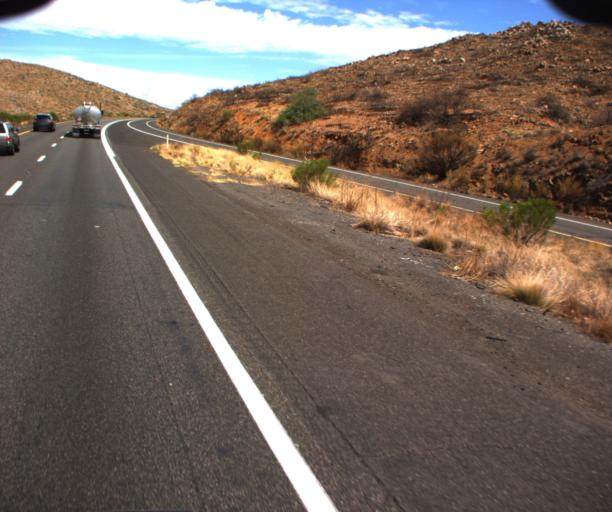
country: US
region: Arizona
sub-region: Yavapai County
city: Cordes Lakes
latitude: 34.2862
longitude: -112.1220
